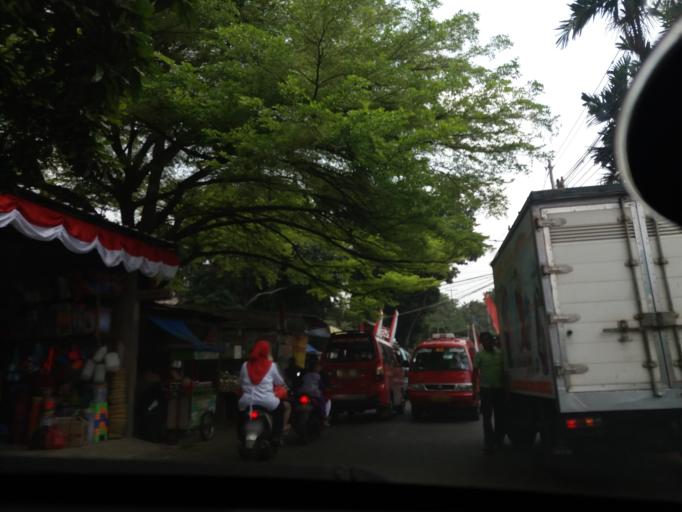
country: ID
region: West Java
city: Depok
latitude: -6.3312
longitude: 106.8321
